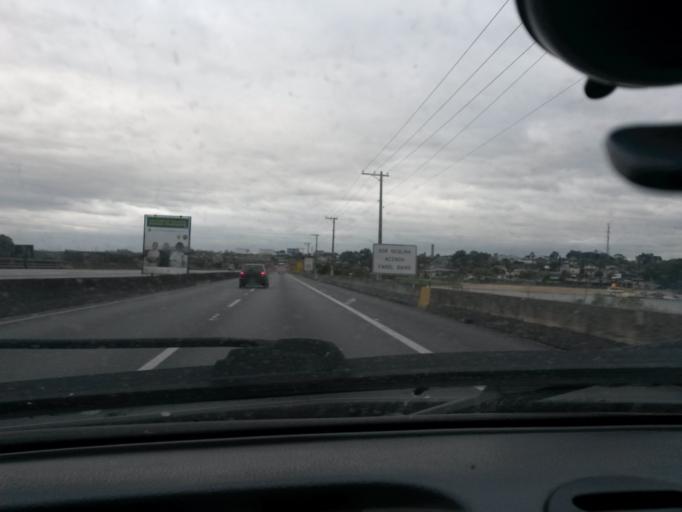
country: BR
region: Sao Paulo
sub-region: Sao Bernardo Do Campo
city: Sao Bernardo do Campo
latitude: -23.7720
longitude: -46.5325
